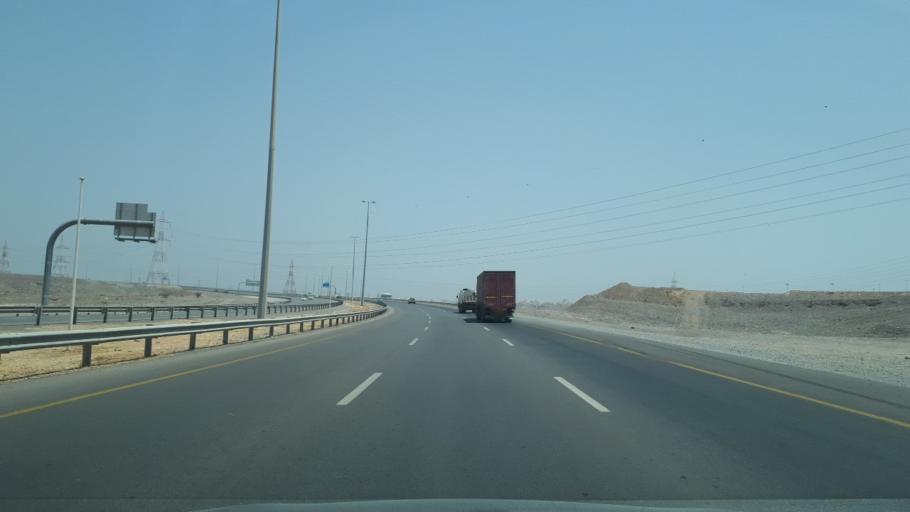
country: OM
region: Muhafazat Masqat
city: As Sib al Jadidah
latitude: 23.6182
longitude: 58.0888
